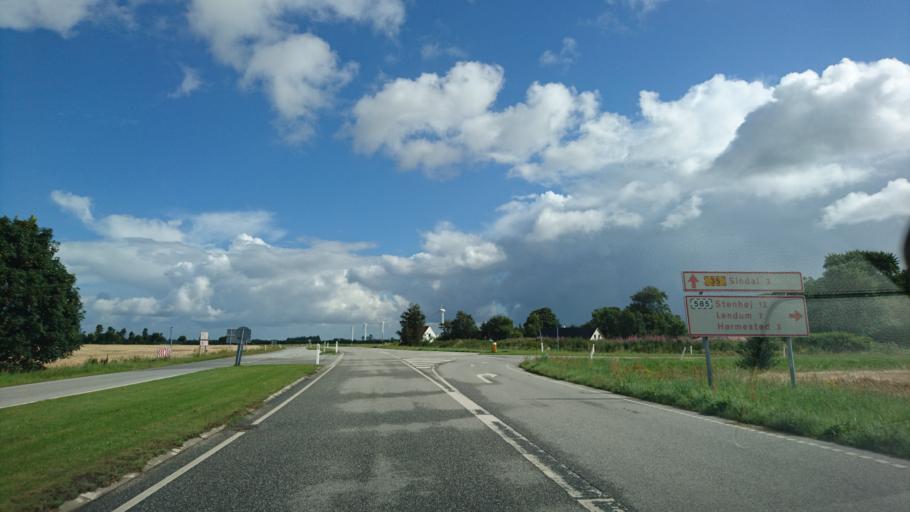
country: DK
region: North Denmark
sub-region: Hjorring Kommune
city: Sindal
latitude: 57.4446
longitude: 10.2075
